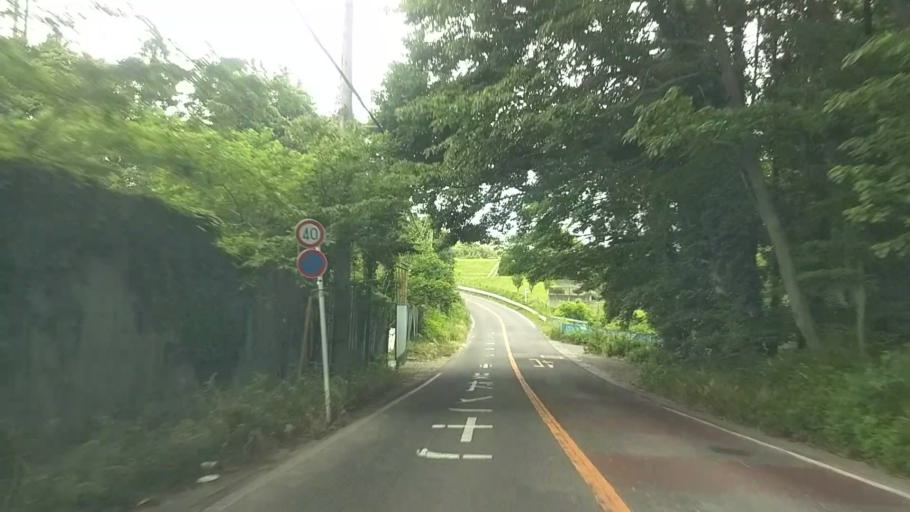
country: JP
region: Kanagawa
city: Fujisawa
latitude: 35.3592
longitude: 139.4355
